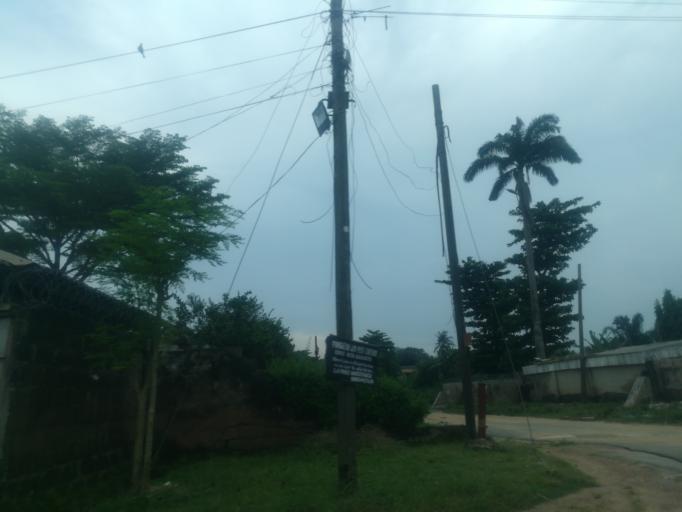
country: NG
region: Oyo
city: Ibadan
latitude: 7.4137
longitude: 3.9032
